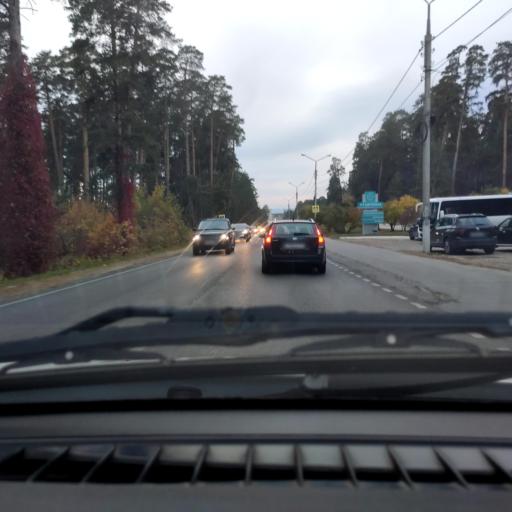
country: RU
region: Samara
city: Tol'yatti
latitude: 53.4758
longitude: 49.3398
